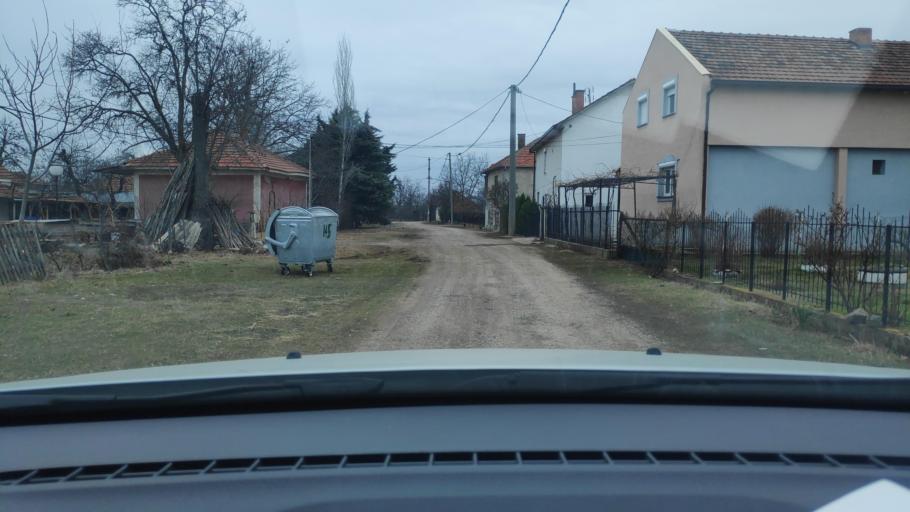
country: MK
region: Opstina Lipkovo
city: Matejche
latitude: 42.0848
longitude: 21.6201
